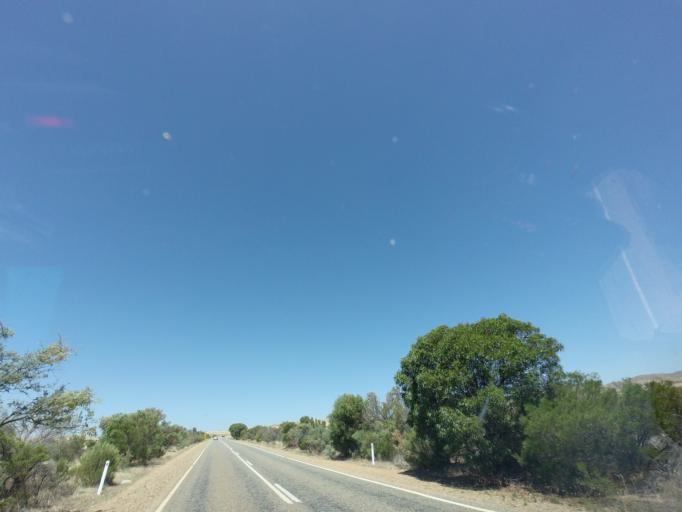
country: AU
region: South Australia
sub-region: Peterborough
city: Peterborough
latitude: -32.7235
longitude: 138.5095
